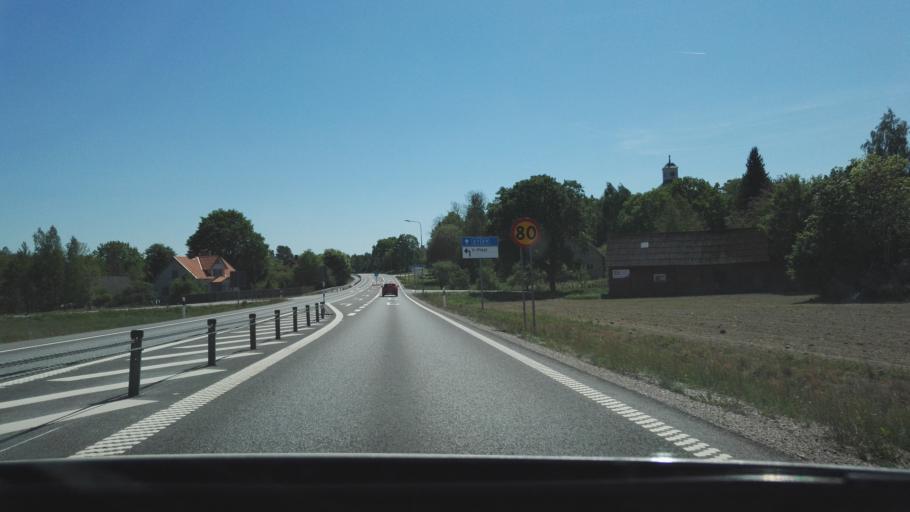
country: SE
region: Kronoberg
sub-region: Vaxjo Kommun
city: Ingelstad
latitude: 56.6494
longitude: 14.9161
